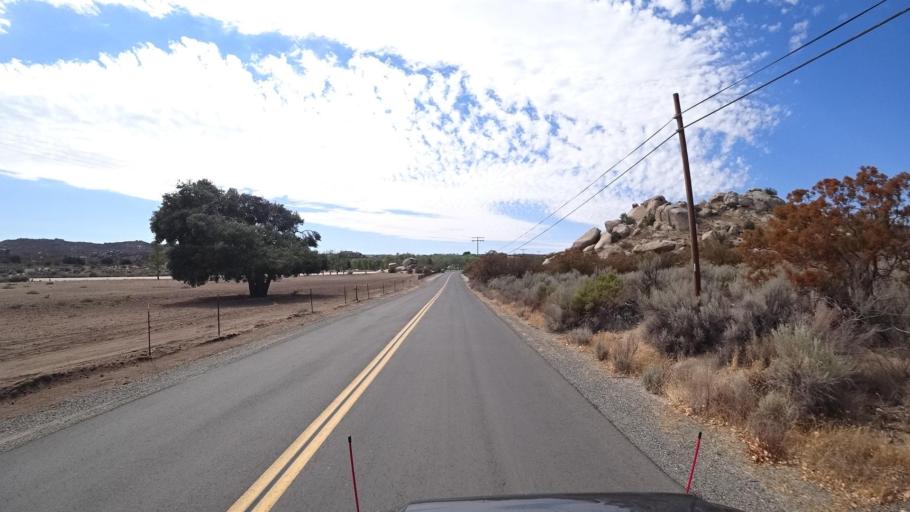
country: MX
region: Baja California
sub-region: Tecate
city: Cereso del Hongo
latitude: 32.6450
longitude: -116.2828
